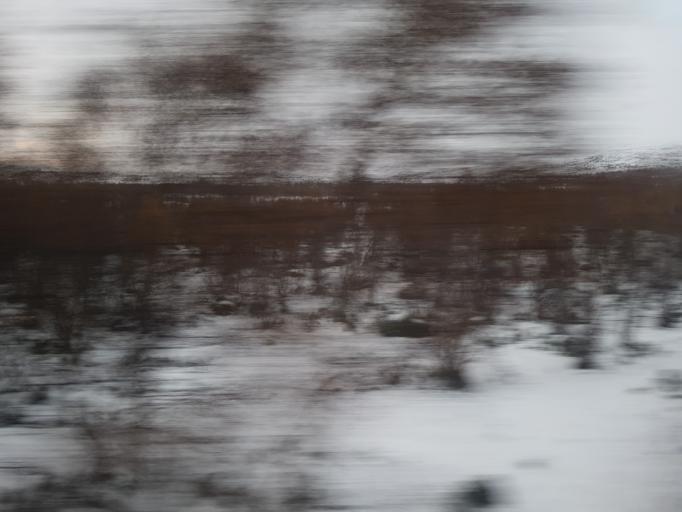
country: NO
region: Oppland
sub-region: Dovre
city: Dovre
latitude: 62.1661
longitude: 9.3848
